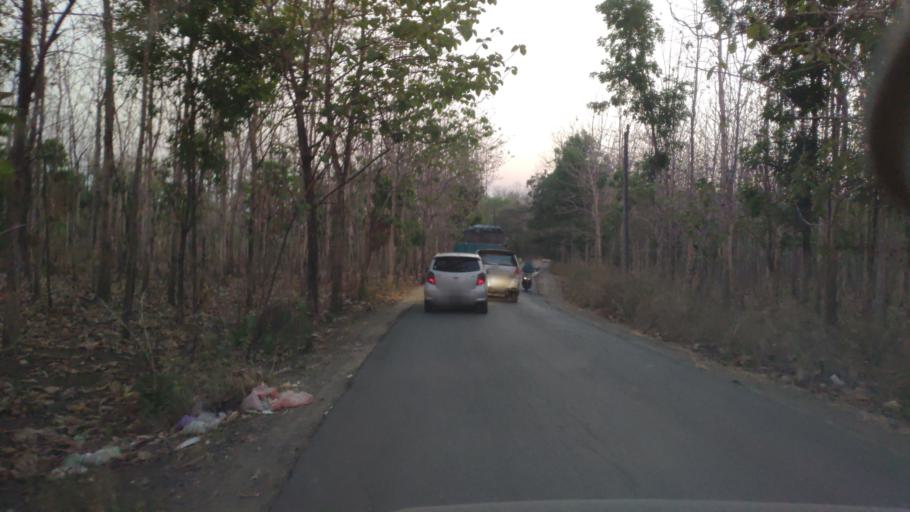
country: ID
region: Central Java
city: Ngliron
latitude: -7.1417
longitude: 111.4205
